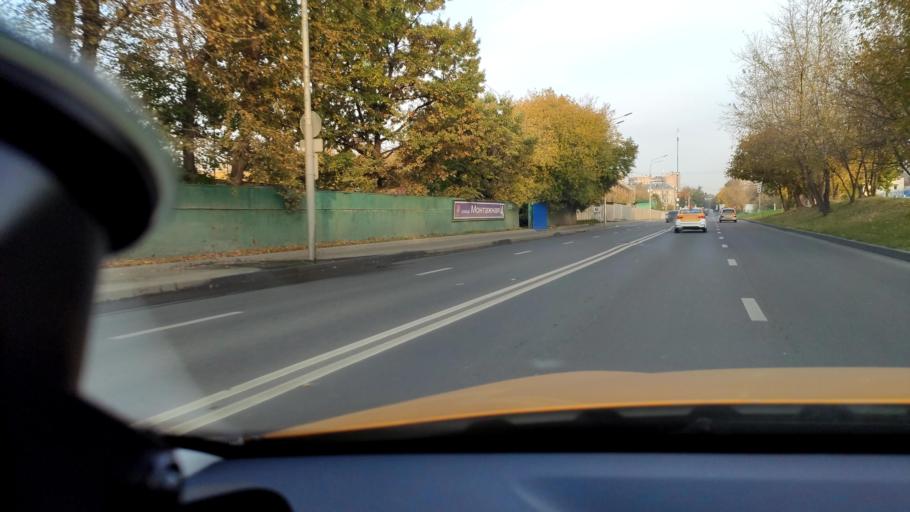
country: RU
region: Moscow
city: Metrogorodok
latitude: 55.8189
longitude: 37.7667
